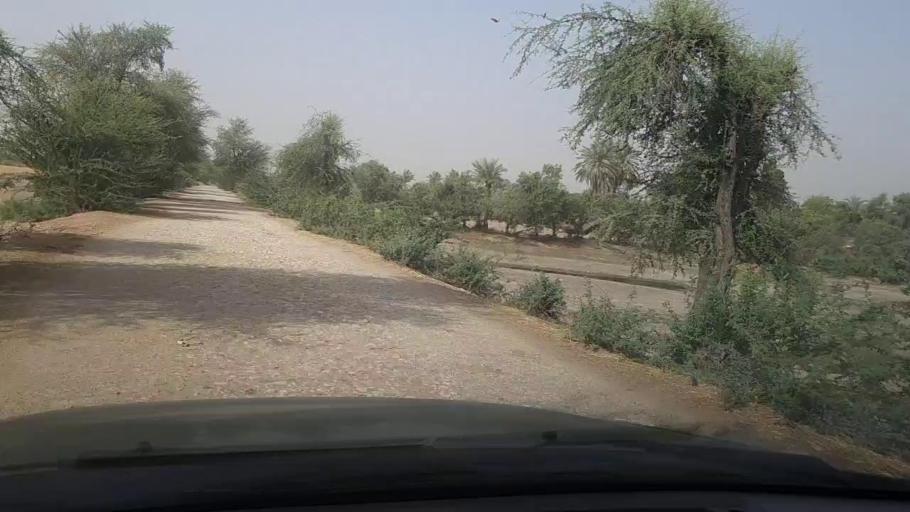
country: PK
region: Sindh
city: Shikarpur
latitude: 27.9055
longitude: 68.5969
